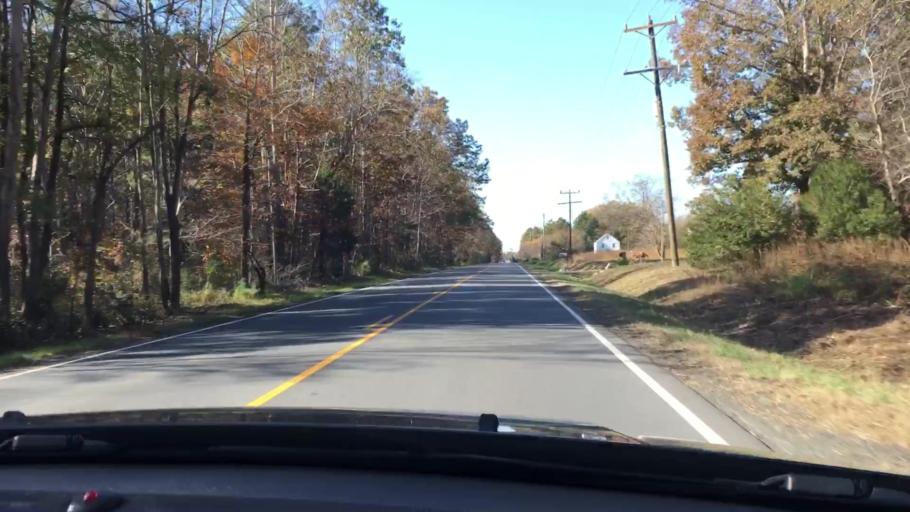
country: US
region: Virginia
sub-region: King William County
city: King William
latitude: 37.6897
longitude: -77.0217
